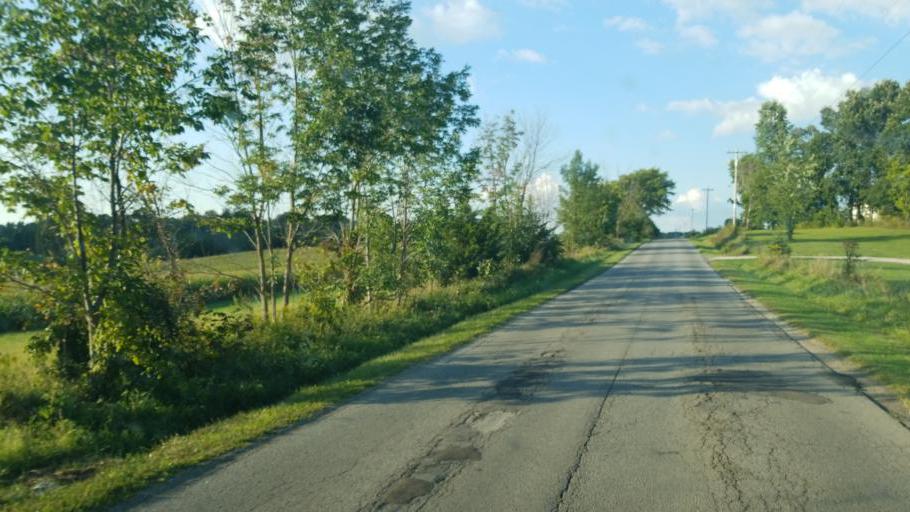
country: US
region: Ohio
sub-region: Morrow County
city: Mount Gilead
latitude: 40.5315
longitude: -82.7404
